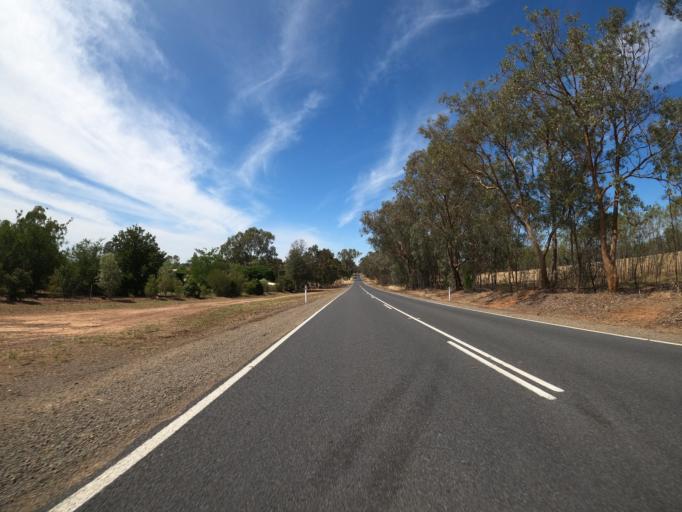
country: AU
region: Victoria
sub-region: Benalla
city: Benalla
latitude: -36.3843
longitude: 145.9787
